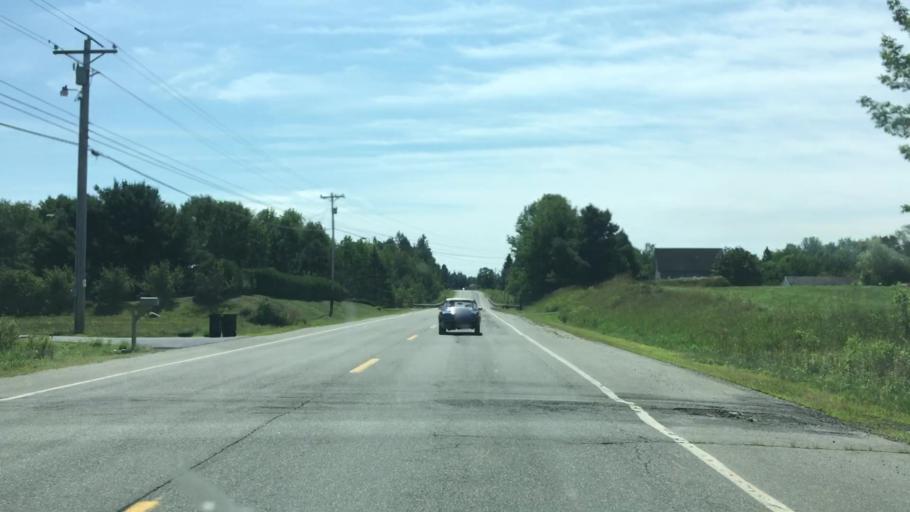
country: CA
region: New Brunswick
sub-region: Charlotte County
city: Saint Andrews
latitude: 45.1042
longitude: -67.1334
